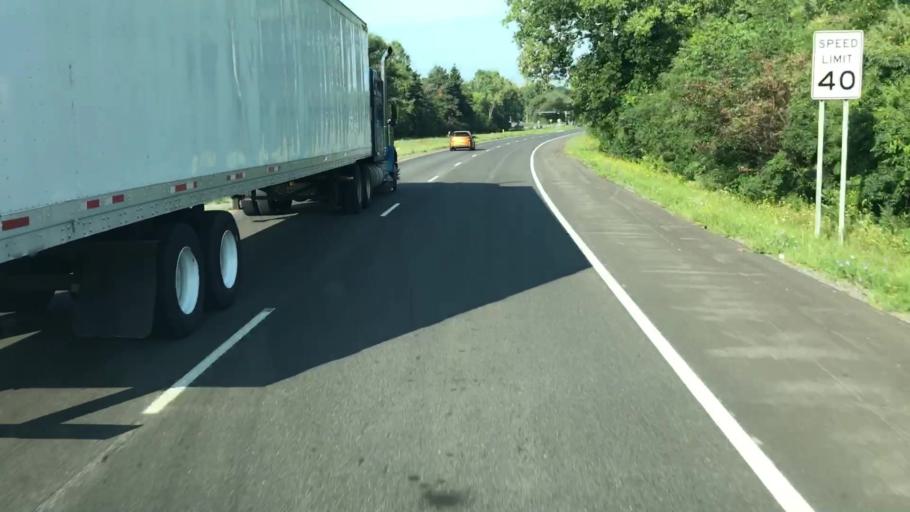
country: US
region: New York
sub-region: Onondaga County
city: Liverpool
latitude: 43.1316
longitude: -76.2155
